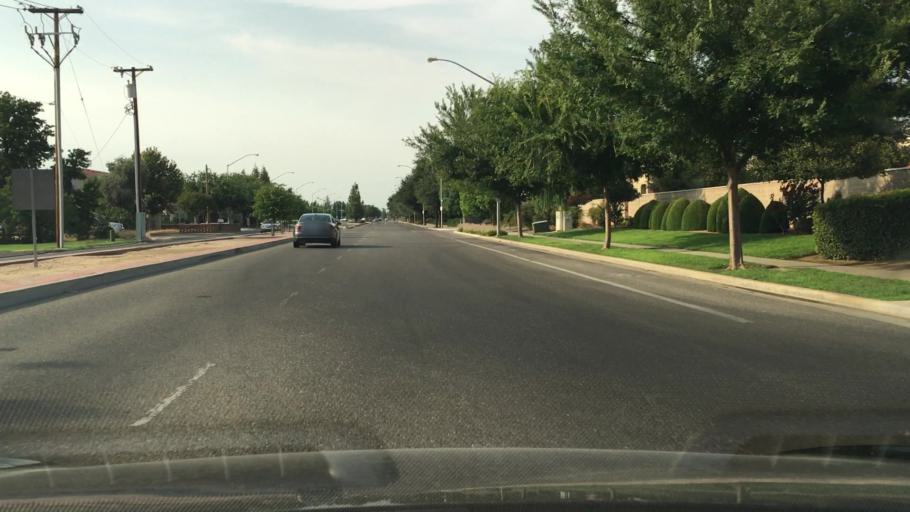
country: US
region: California
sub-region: Fresno County
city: Clovis
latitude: 36.8622
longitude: -119.7387
